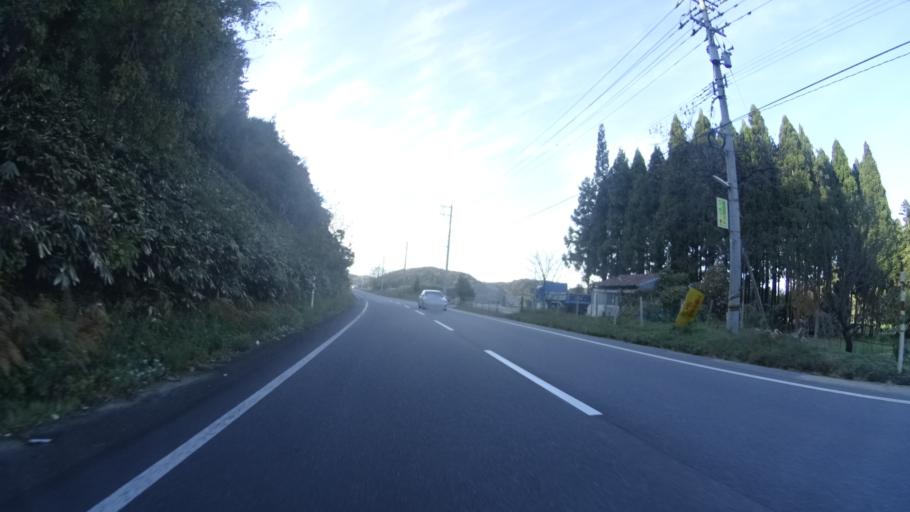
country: JP
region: Ishikawa
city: Hakui
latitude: 37.0160
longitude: 136.7950
